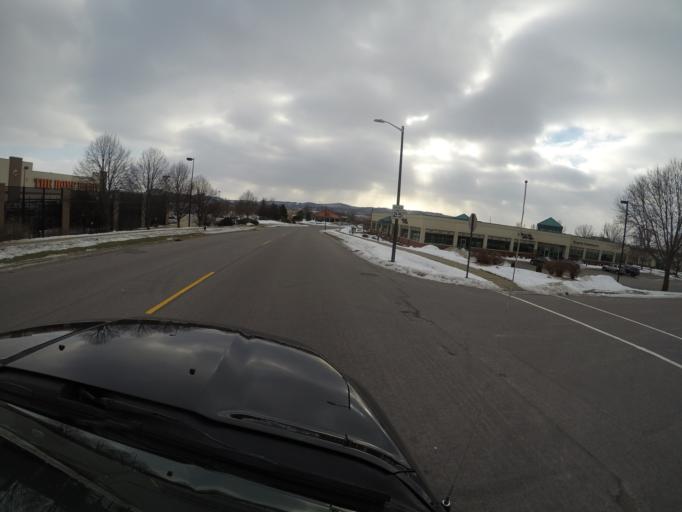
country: US
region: Wisconsin
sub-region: La Crosse County
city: Onalaska
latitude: 43.8803
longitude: -91.1878
